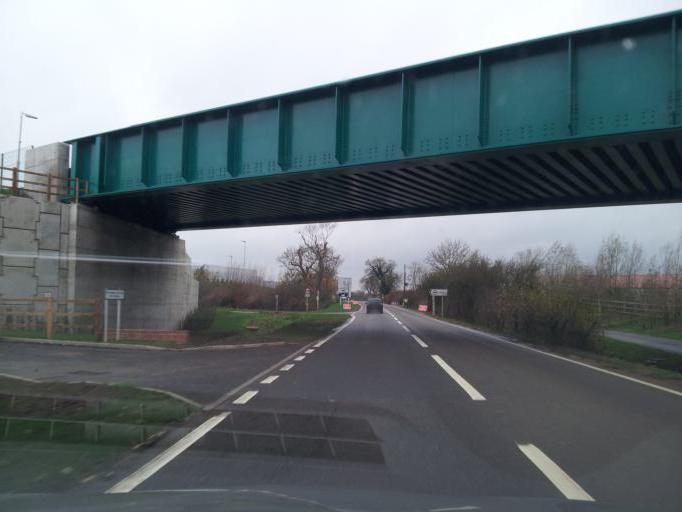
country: GB
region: England
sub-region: Warwickshire
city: Rugby
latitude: 52.3540
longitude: -1.1774
